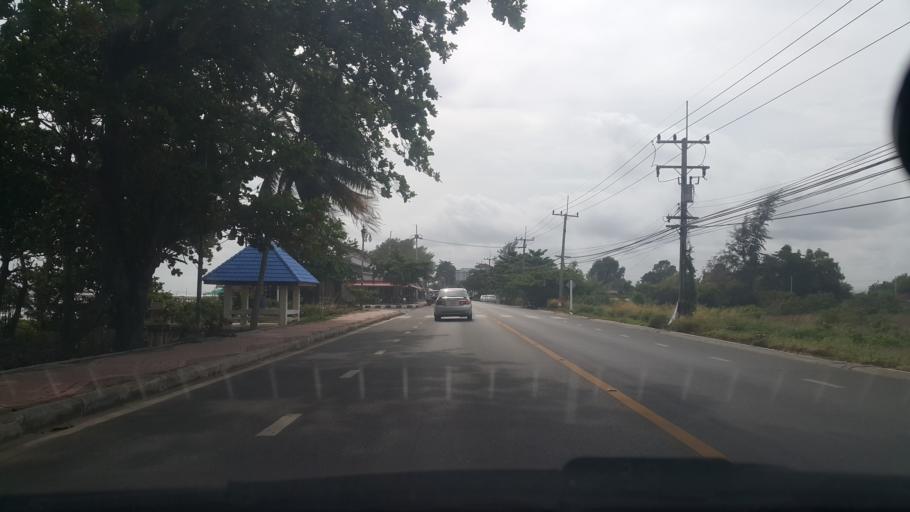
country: TH
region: Rayong
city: Rayong
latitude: 12.6269
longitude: 101.3540
